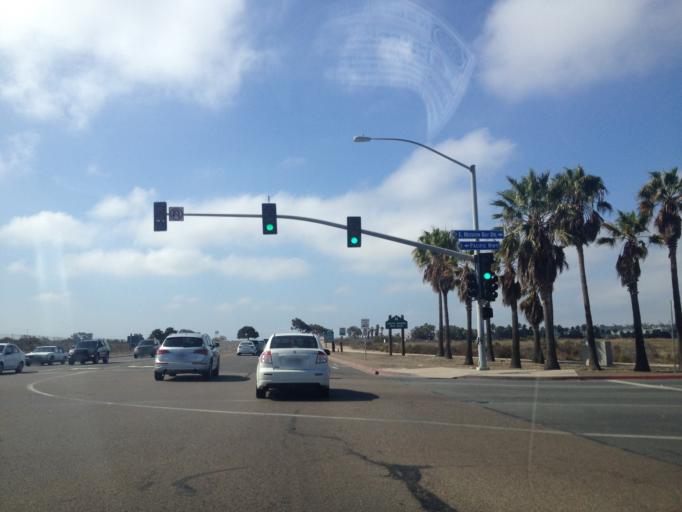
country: US
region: California
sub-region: San Diego County
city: San Diego
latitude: 32.7674
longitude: -117.2088
